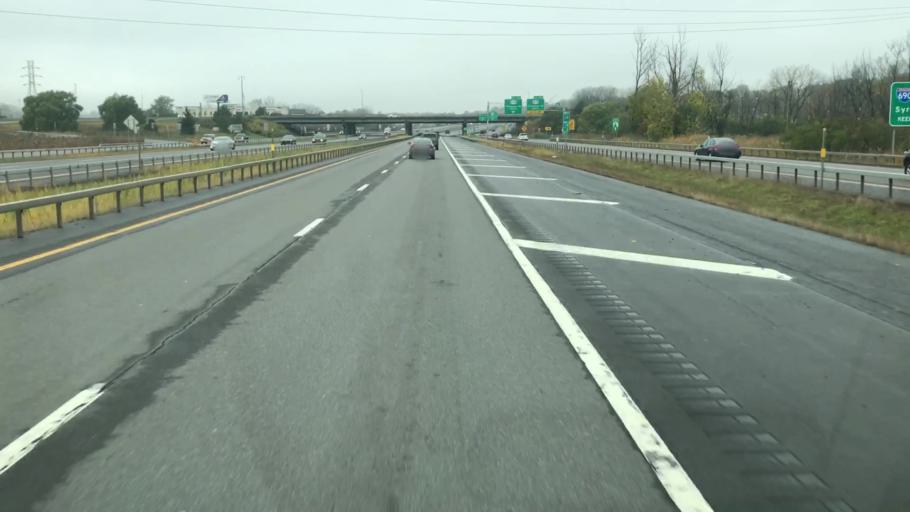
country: US
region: New York
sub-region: Onondaga County
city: East Syracuse
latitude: 43.0582
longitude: -76.0795
